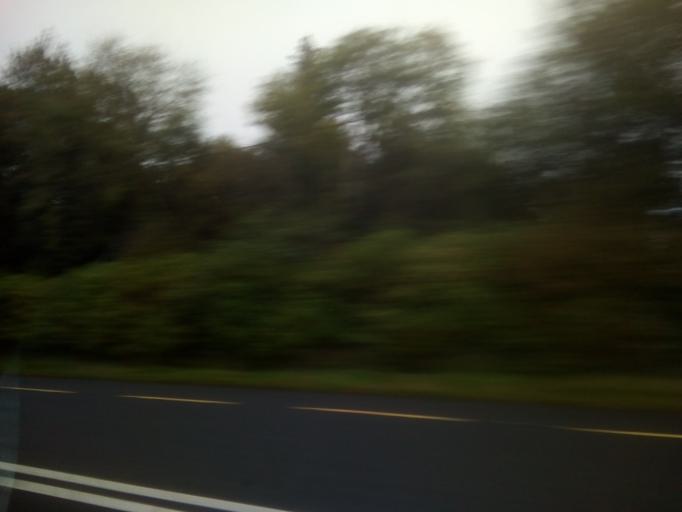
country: IE
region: Leinster
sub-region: An Iarmhi
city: An Muileann gCearr
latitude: 53.5724
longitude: -7.3634
